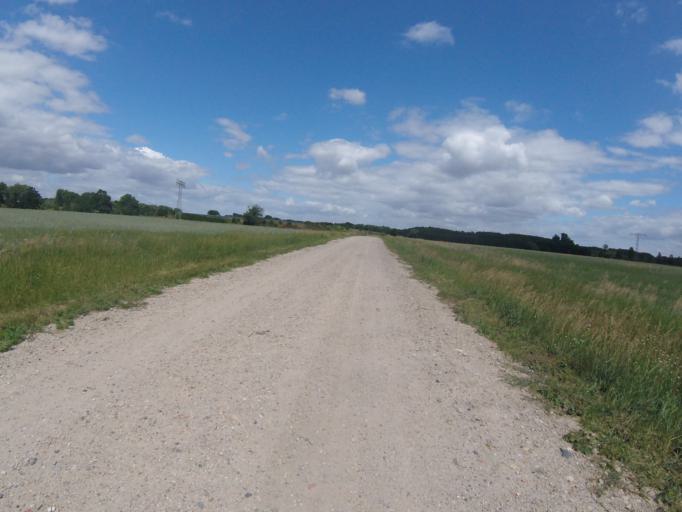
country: DE
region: Brandenburg
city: Mittenwalde
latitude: 52.2468
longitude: 13.5340
